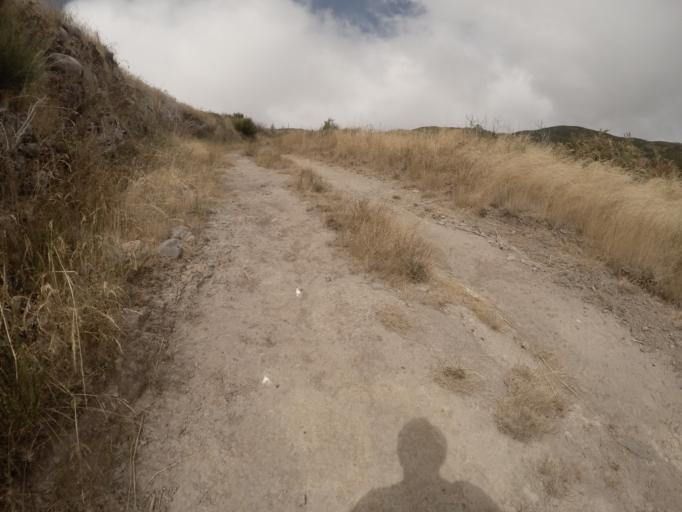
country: PT
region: Madeira
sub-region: Camara de Lobos
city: Curral das Freiras
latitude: 32.7085
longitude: -16.9981
